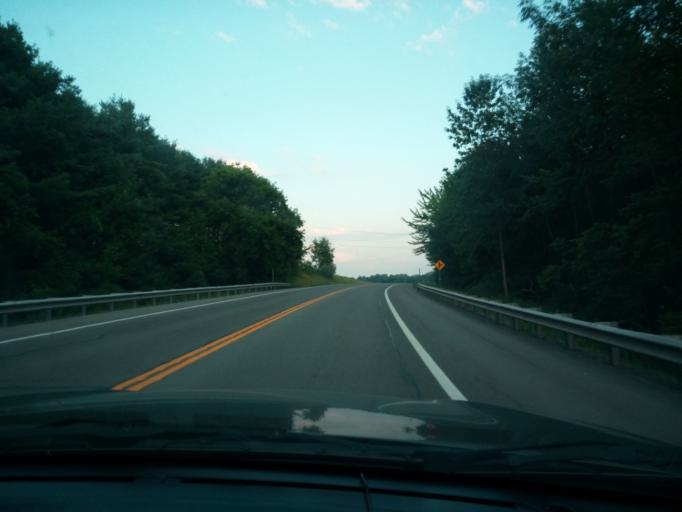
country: US
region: New York
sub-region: Wayne County
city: Clyde
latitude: 43.0719
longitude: -76.7776
